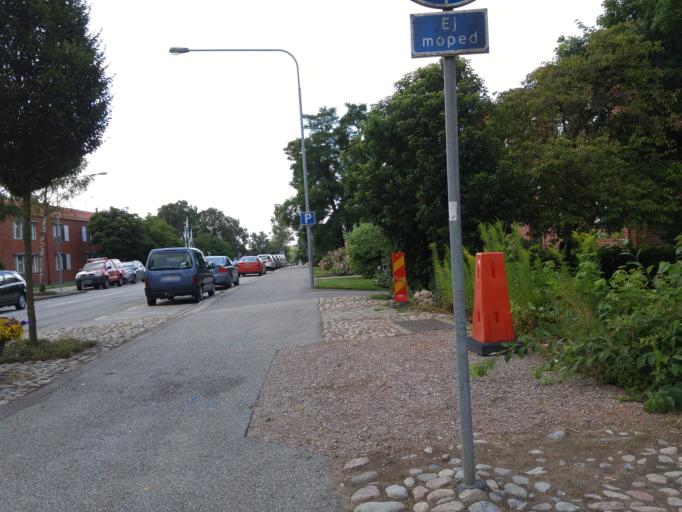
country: SE
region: Skane
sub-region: Hoors Kommun
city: Hoeoer
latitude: 55.9329
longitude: 13.5413
